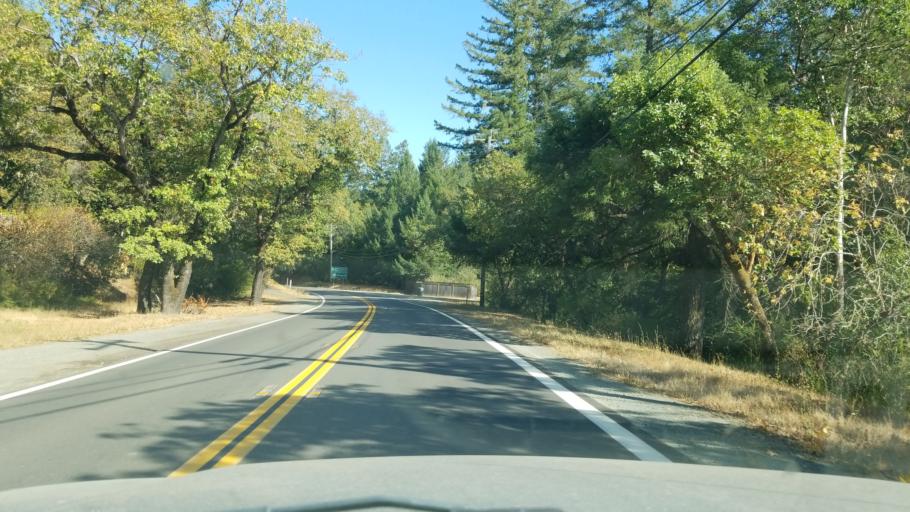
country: US
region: California
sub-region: Humboldt County
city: Redway
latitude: 40.2192
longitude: -123.8147
